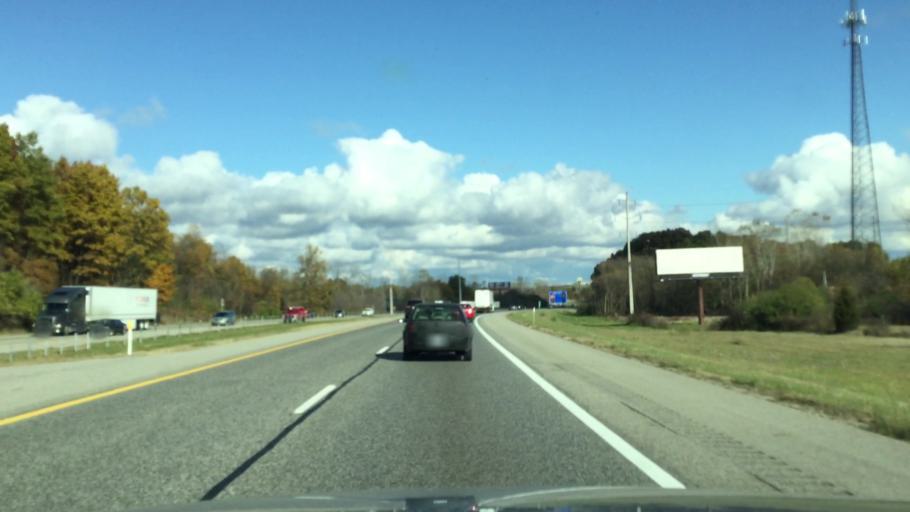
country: US
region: Michigan
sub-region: Berrien County
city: Coloma
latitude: 42.1735
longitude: -86.3147
